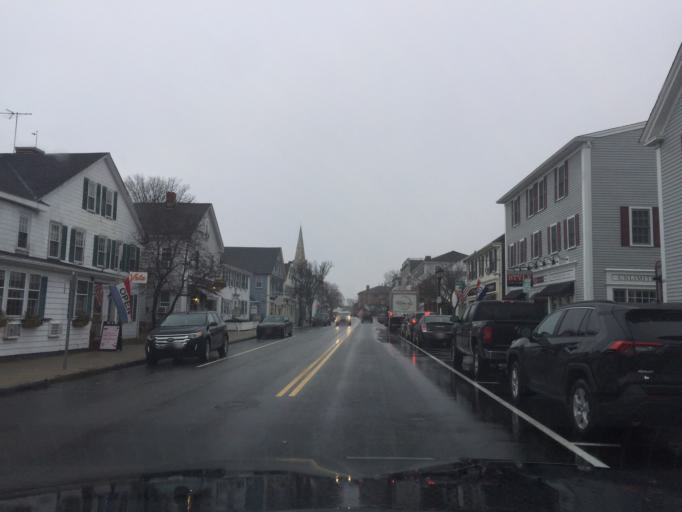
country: US
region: Massachusetts
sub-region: Plymouth County
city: Plymouth
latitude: 41.9588
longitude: -70.6682
